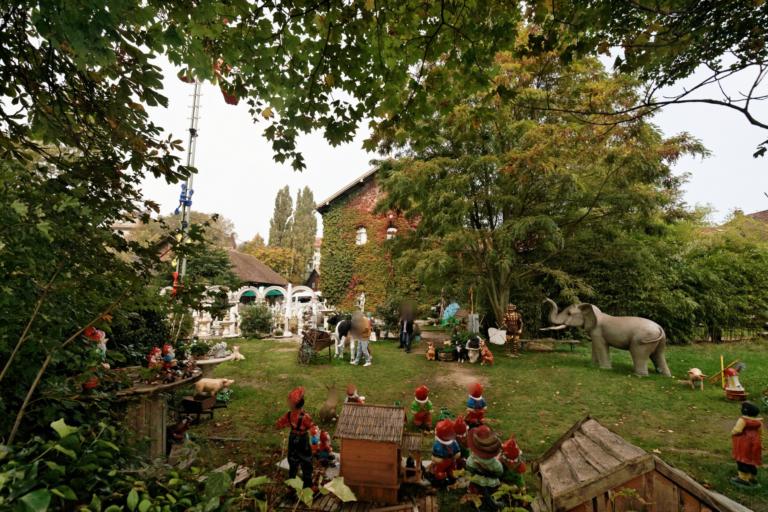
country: DE
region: Bavaria
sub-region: Swabia
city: Lindau
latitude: 47.5440
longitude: 9.6785
